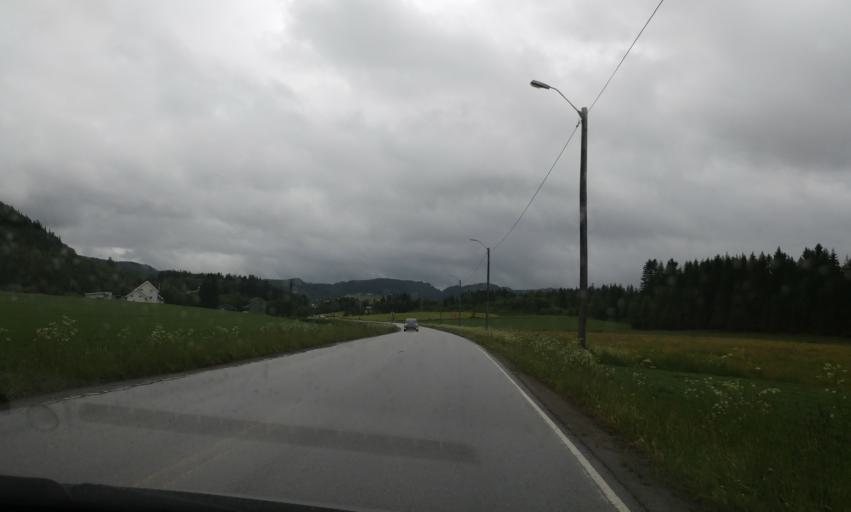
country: NO
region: Sor-Trondelag
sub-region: Selbu
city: Mebonden
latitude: 63.2666
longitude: 11.0792
